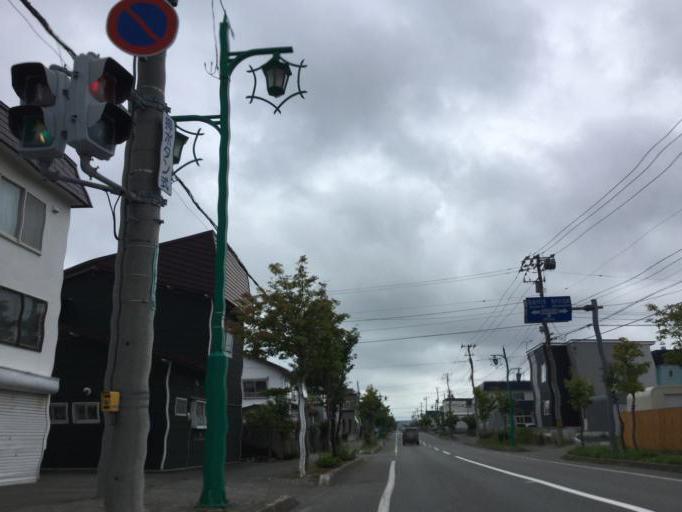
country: JP
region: Hokkaido
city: Wakkanai
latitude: 45.3907
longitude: 141.6997
